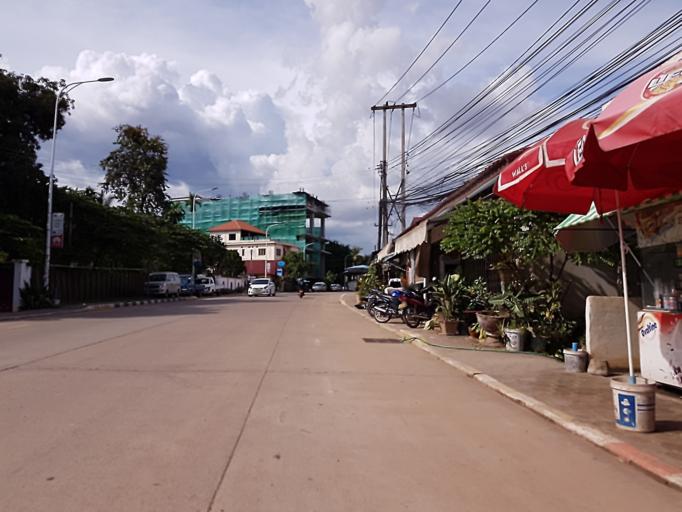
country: LA
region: Vientiane
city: Vientiane
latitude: 17.9324
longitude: 102.6250
